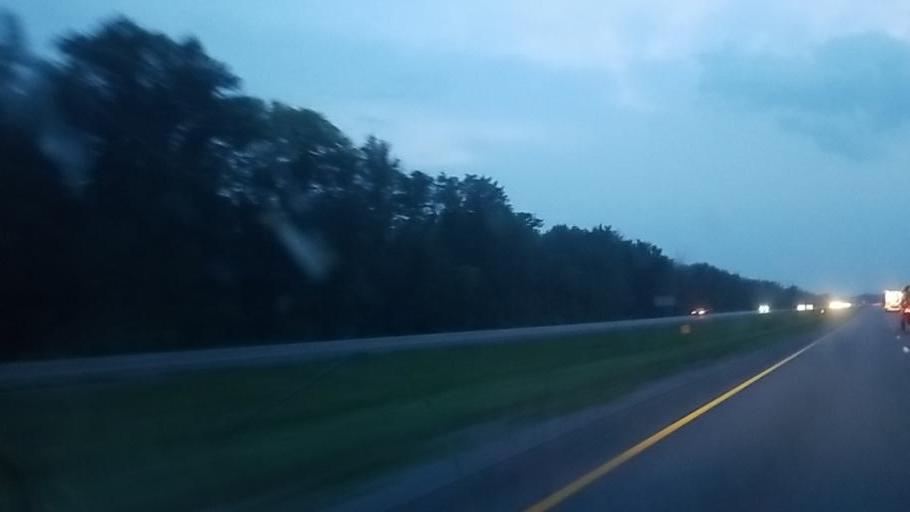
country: US
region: New York
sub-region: Onondaga County
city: Minoa
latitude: 43.0948
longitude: -76.0140
